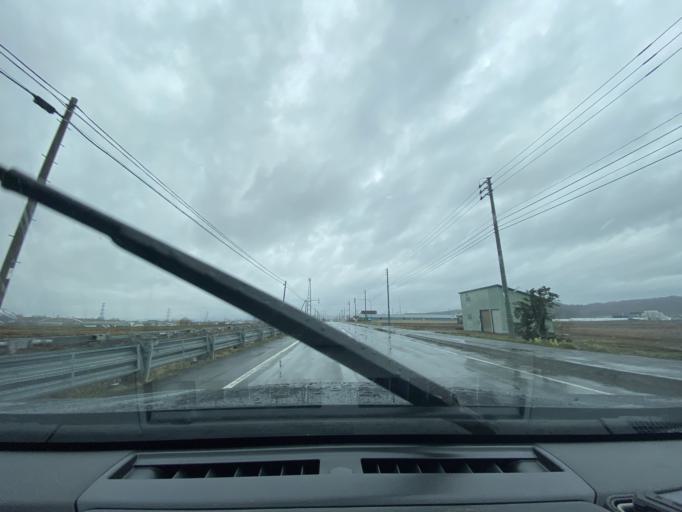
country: JP
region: Hokkaido
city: Fukagawa
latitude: 43.8162
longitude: 141.9898
